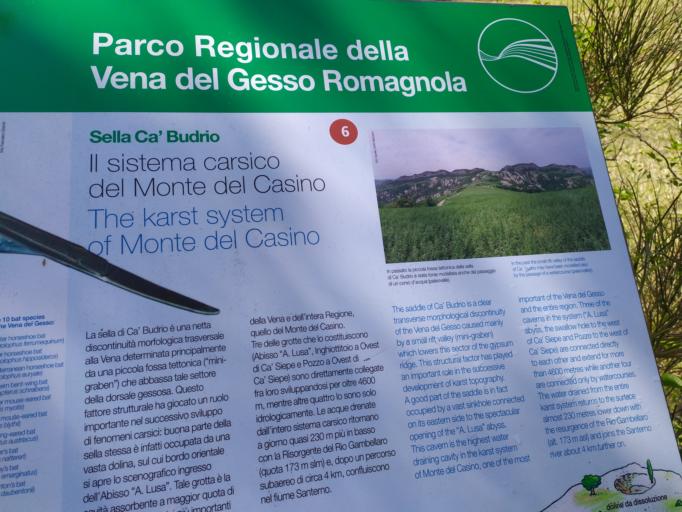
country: IT
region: Emilia-Romagna
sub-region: Provincia di Ravenna
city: Casola Valsenio
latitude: 44.2596
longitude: 11.6361
